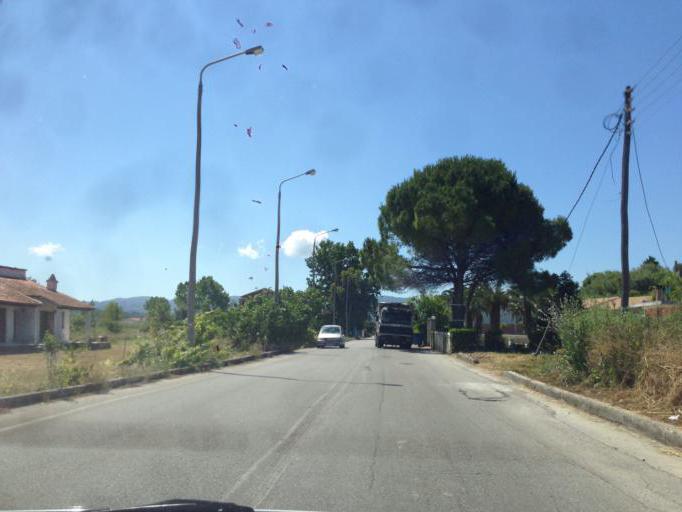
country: GR
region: Ionian Islands
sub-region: Nomos Kerkyras
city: Agios Georgis
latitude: 39.7778
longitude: 19.7102
